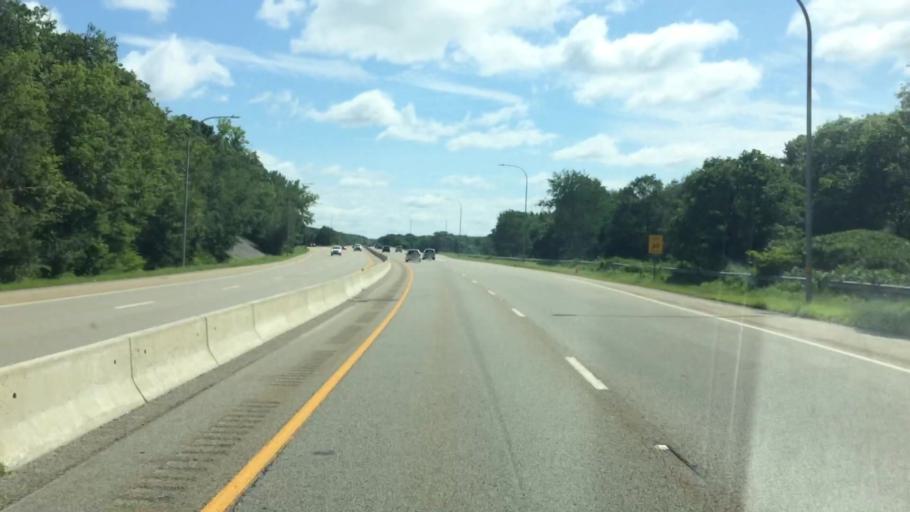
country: US
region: Rhode Island
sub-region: Providence County
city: Cumberland Hill
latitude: 41.9696
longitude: -71.4856
